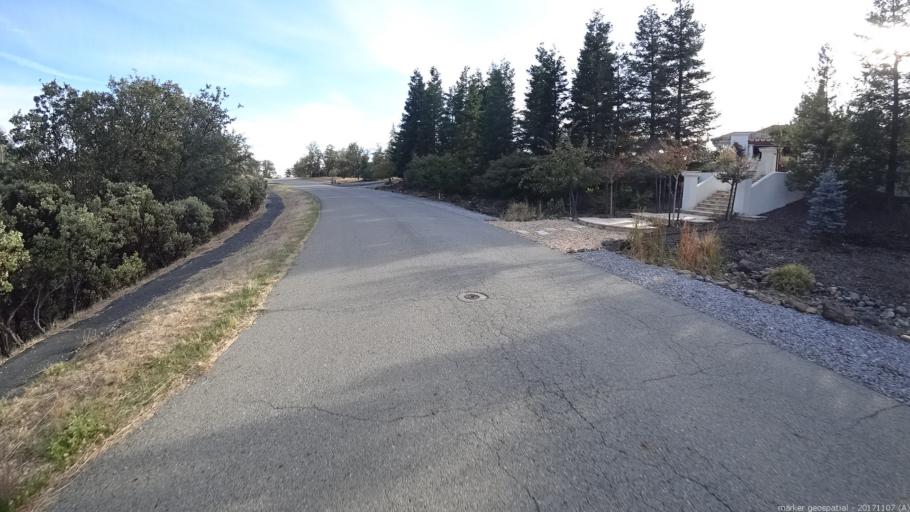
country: US
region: California
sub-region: Shasta County
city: Shasta
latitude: 40.5084
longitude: -122.4735
